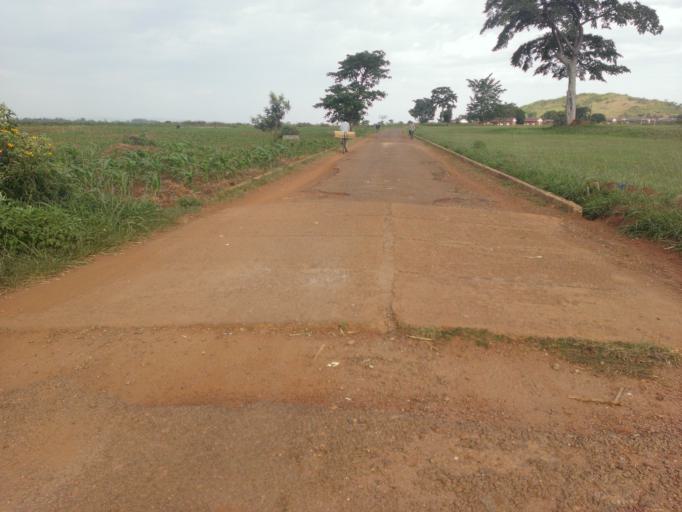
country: UG
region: Eastern Region
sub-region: Busia District
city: Busia
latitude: 0.5486
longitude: 34.0219
